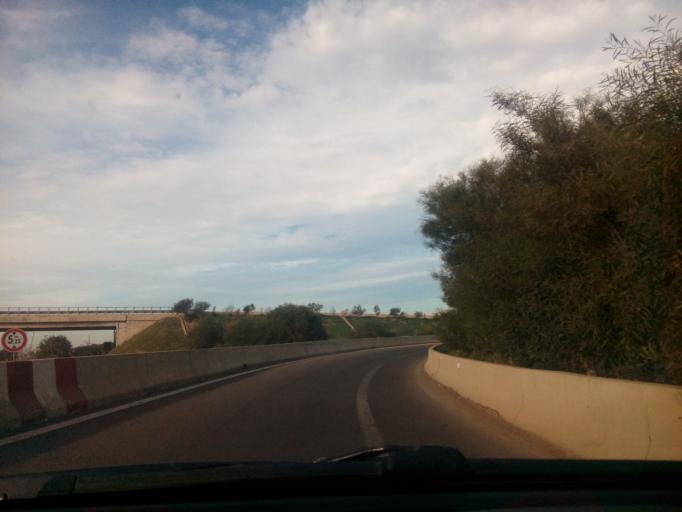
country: DZ
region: Mascara
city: Sig
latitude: 35.5827
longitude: -0.2192
